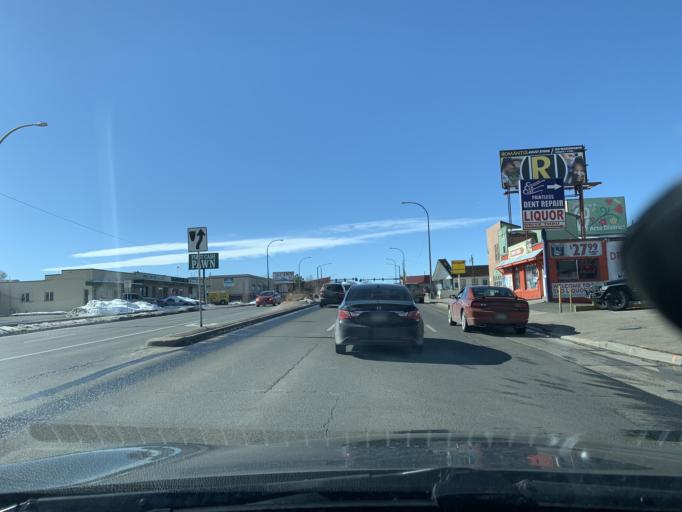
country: US
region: Colorado
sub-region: Jefferson County
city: Edgewater
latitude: 39.7404
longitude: -105.0742
